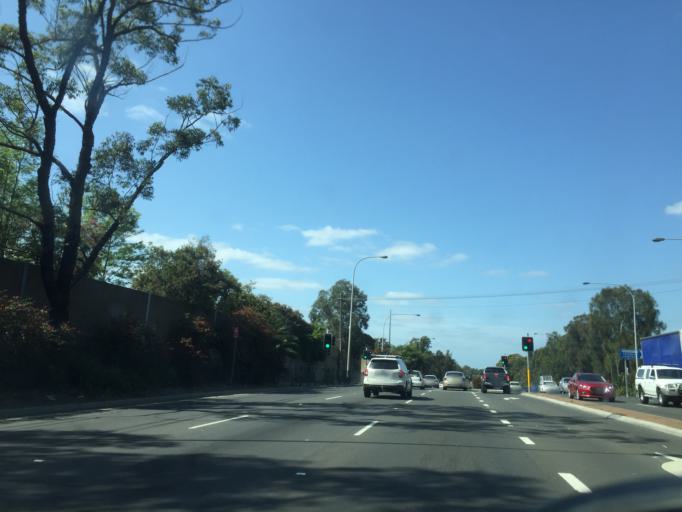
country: AU
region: New South Wales
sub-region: Strathfield
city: Homebush
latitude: -33.8748
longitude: 151.0671
